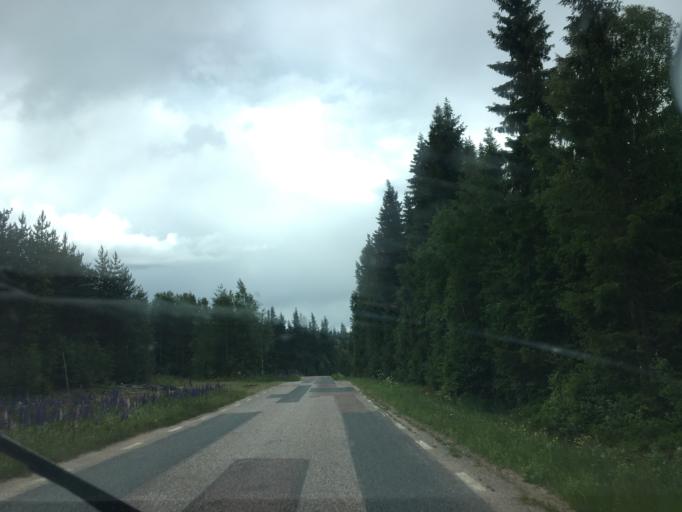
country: SE
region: OErebro
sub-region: Hallefors Kommun
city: Haellefors
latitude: 60.0554
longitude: 14.4977
